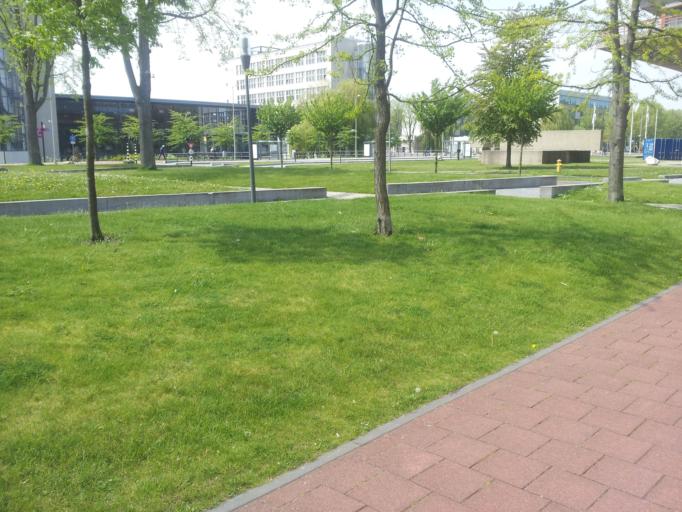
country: NL
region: South Holland
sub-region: Gemeente Delft
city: Delft
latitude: 52.0015
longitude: 4.3734
